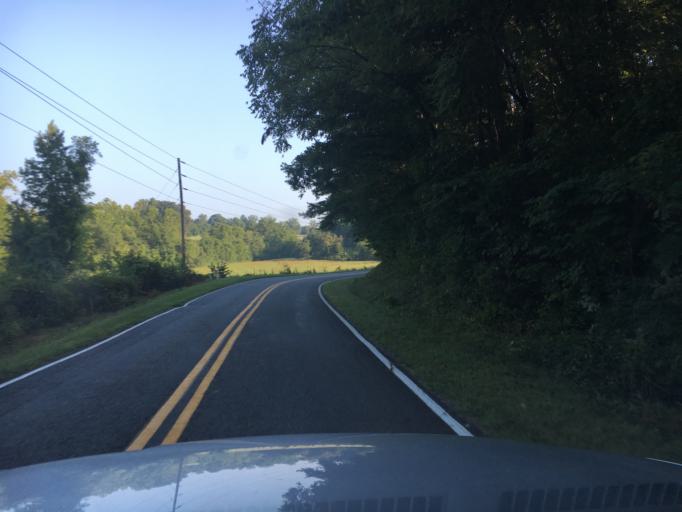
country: US
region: North Carolina
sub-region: Rutherford County
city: Rutherfordton
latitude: 35.2560
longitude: -82.0314
